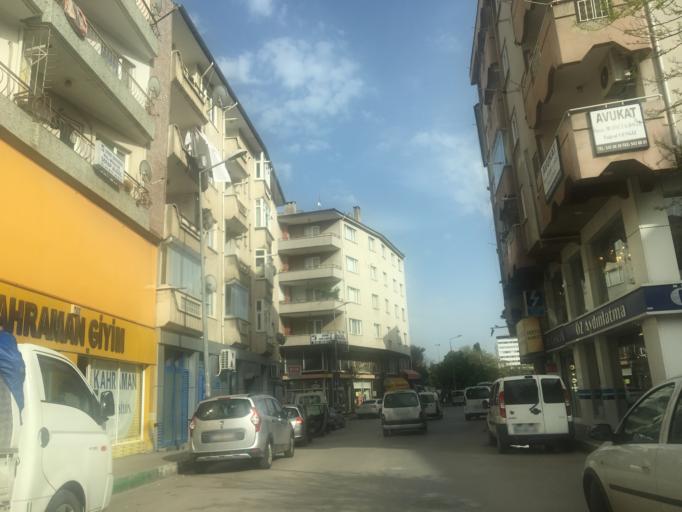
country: TR
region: Bursa
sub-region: Mudanya
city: Mudanya
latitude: 40.3745
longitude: 28.8866
